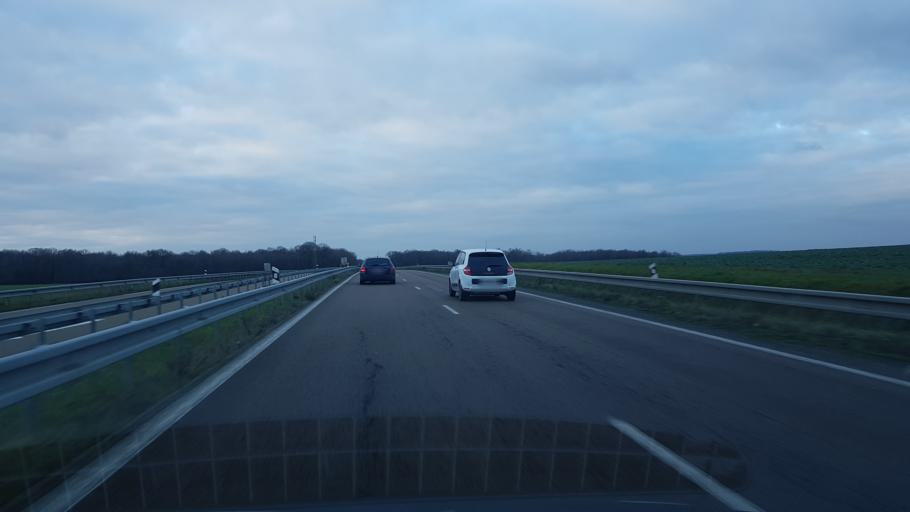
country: FR
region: Champagne-Ardenne
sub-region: Departement de la Marne
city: Sezanne
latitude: 48.7286
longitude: 3.6636
